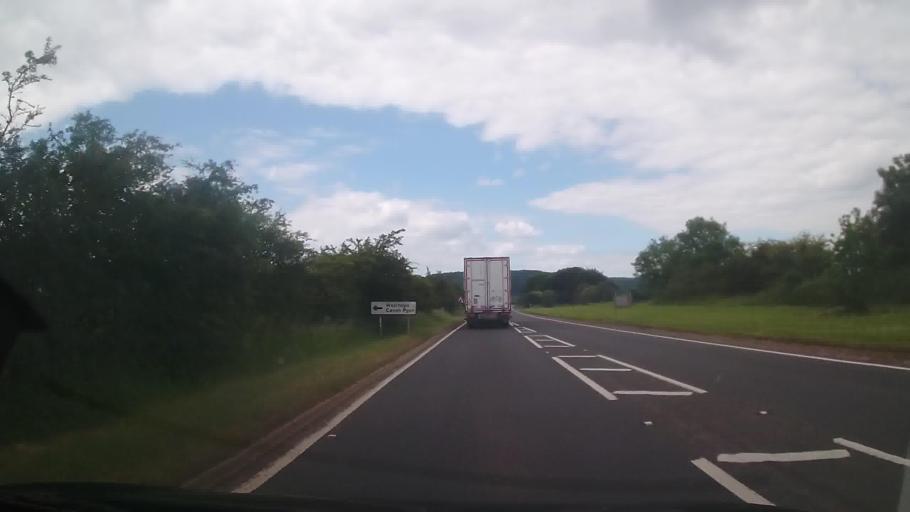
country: GB
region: England
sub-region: Herefordshire
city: Wellington
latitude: 52.1367
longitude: -2.7304
